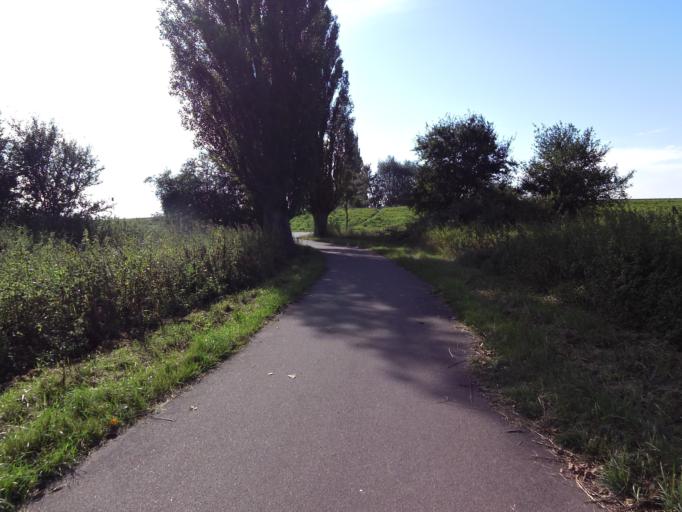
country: DE
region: Saxony-Anhalt
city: Wittenburg
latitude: 51.8638
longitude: 12.5955
